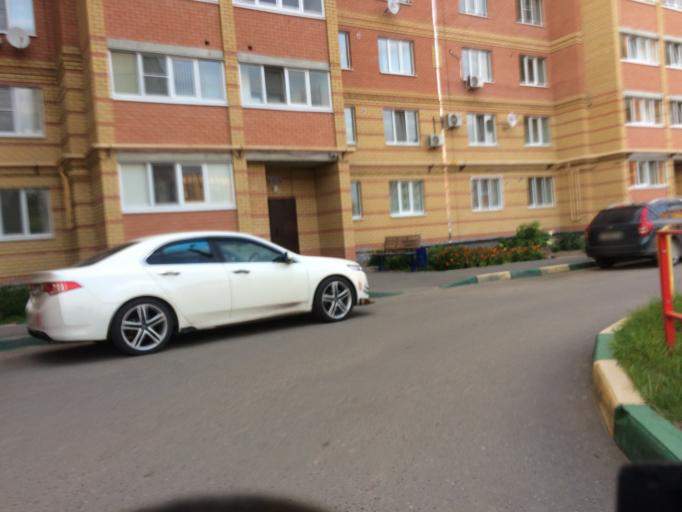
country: RU
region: Mariy-El
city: Yoshkar-Ola
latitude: 56.6441
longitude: 47.8482
